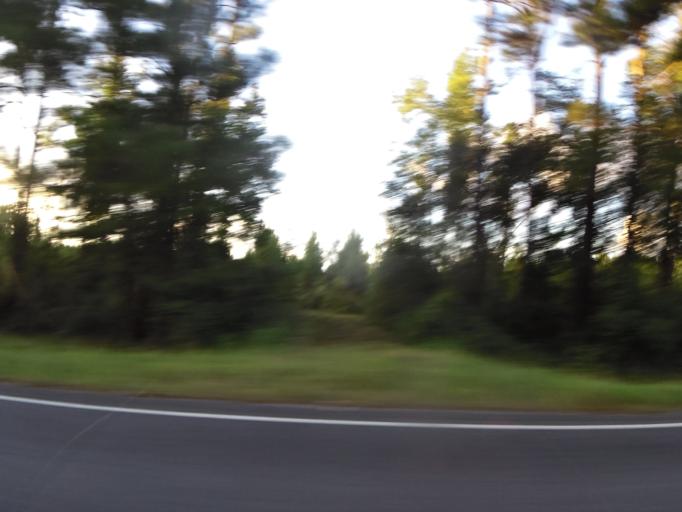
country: US
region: Georgia
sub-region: Camden County
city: Woodbine
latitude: 31.1005
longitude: -81.7064
